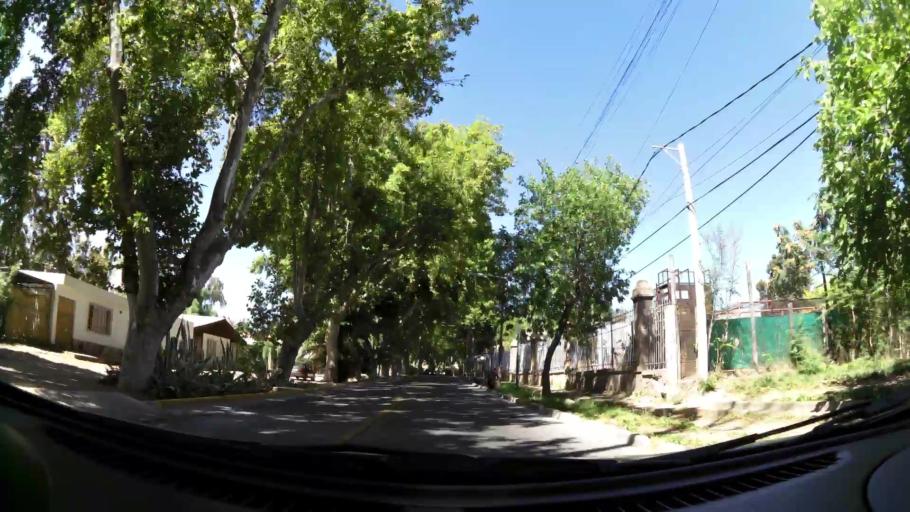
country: AR
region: Mendoza
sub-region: Departamento de Godoy Cruz
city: Godoy Cruz
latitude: -32.9480
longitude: -68.8494
